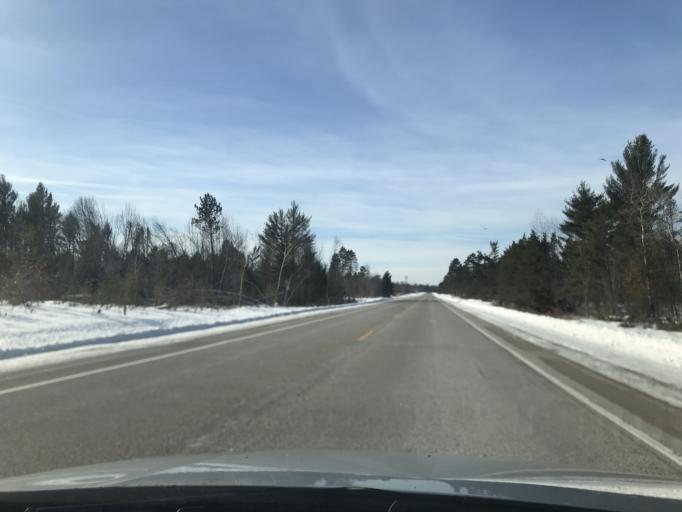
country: US
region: Wisconsin
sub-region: Oconto County
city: Gillett
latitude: 45.1146
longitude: -88.3595
